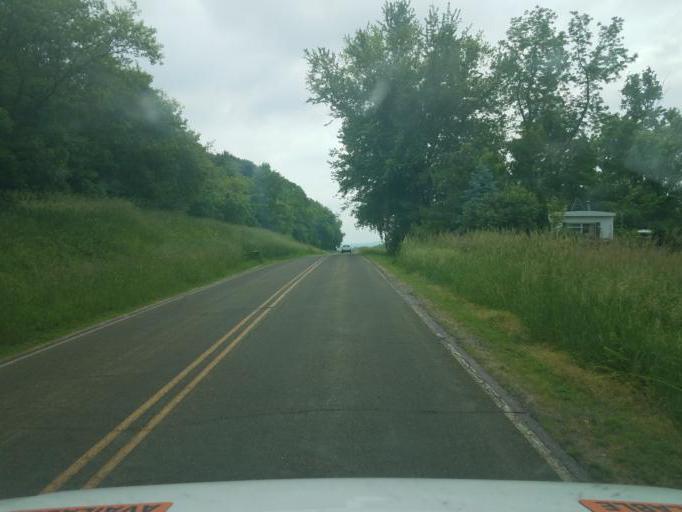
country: US
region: Wisconsin
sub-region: Vernon County
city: Hillsboro
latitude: 43.6453
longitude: -90.2886
